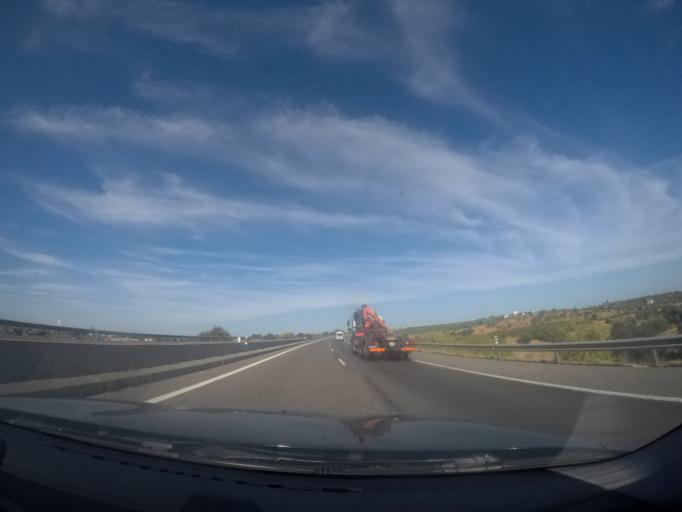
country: PT
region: Faro
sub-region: Silves
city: Armacao de Pera
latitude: 37.1395
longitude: -8.3773
